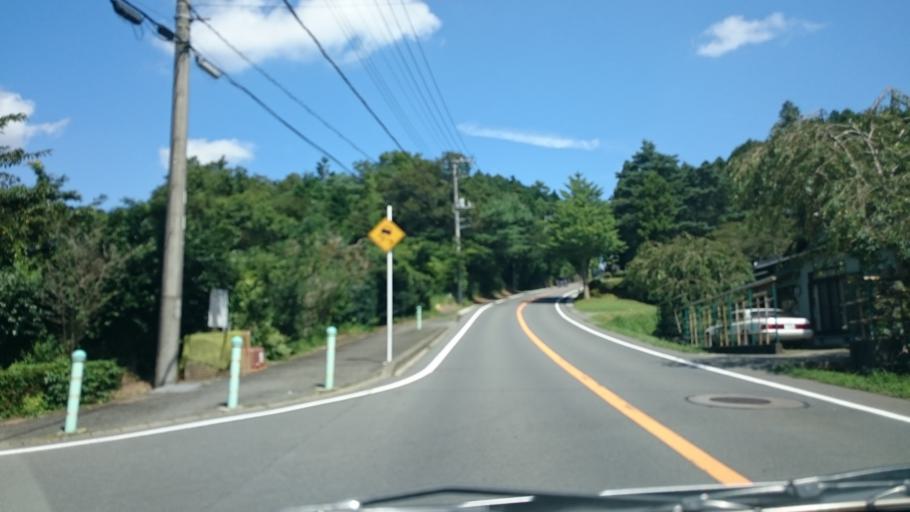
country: JP
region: Shizuoka
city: Gotemba
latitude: 35.2808
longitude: 138.9351
